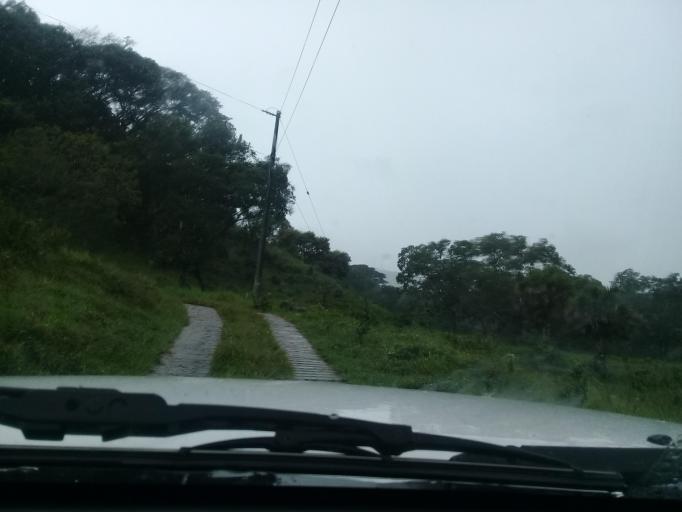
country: MX
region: Veracruz
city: Santiago Tuxtla
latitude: 18.4603
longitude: -95.3252
